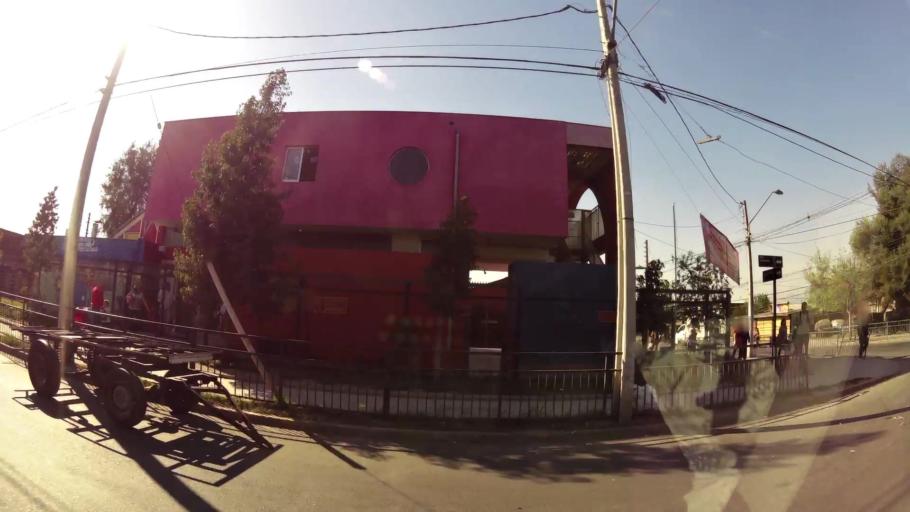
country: CL
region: Santiago Metropolitan
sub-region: Provincia de Santiago
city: La Pintana
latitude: -33.5593
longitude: -70.6062
